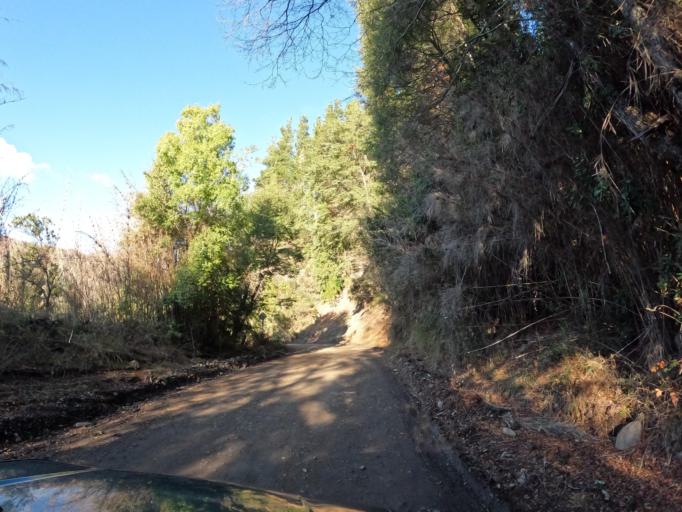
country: CL
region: Biobio
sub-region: Provincia de Nuble
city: Coihueco
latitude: -36.8056
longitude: -71.6439
